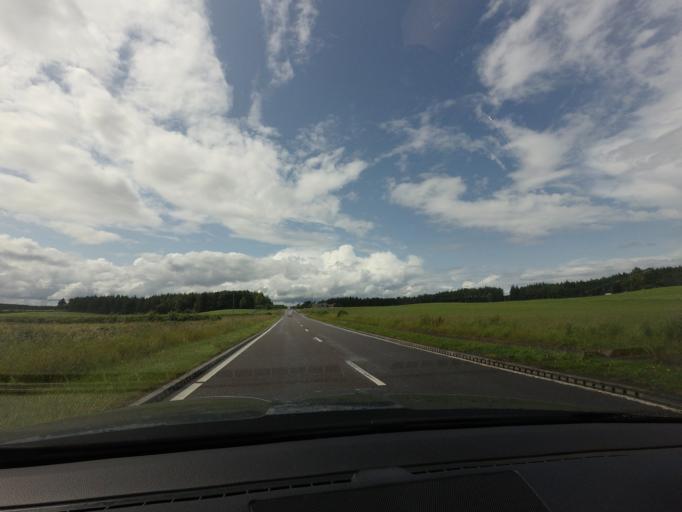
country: GB
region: Scotland
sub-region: Moray
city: Fochabers
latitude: 57.6266
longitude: -3.1550
